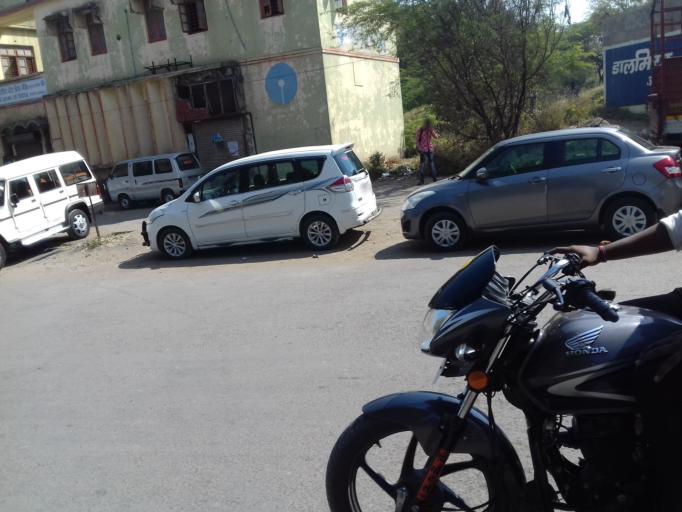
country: IN
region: Maharashtra
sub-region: Solapur
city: Sangola
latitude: 17.4375
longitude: 75.1907
